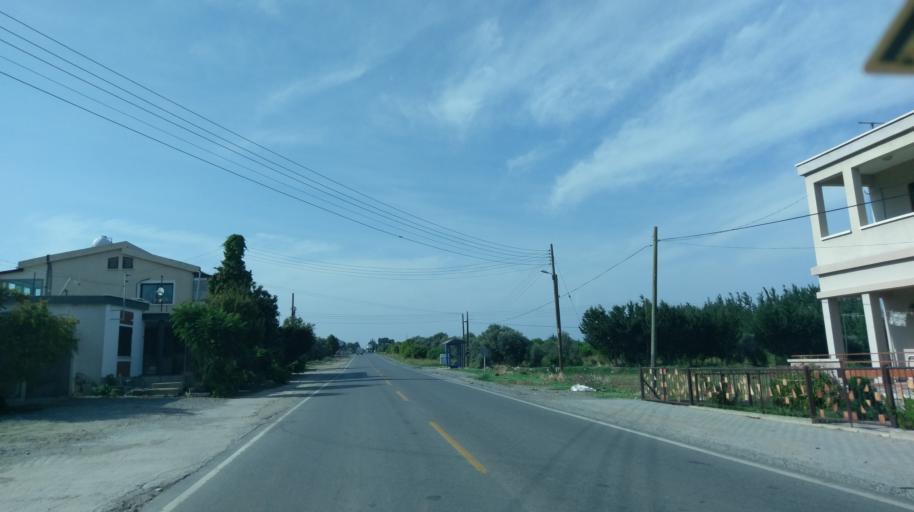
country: CY
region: Keryneia
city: Lapithos
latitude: 35.3521
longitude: 33.1287
